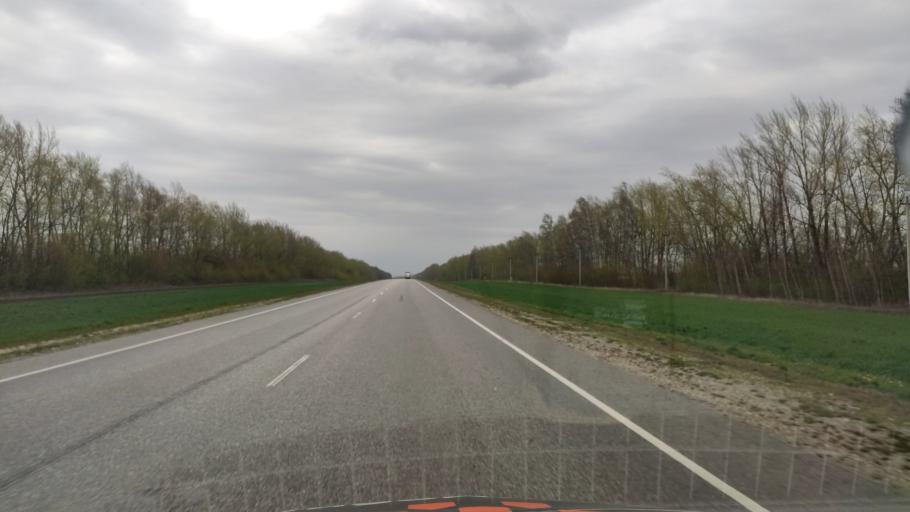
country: RU
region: Kursk
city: Olym
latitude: 51.5497
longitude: 38.1674
